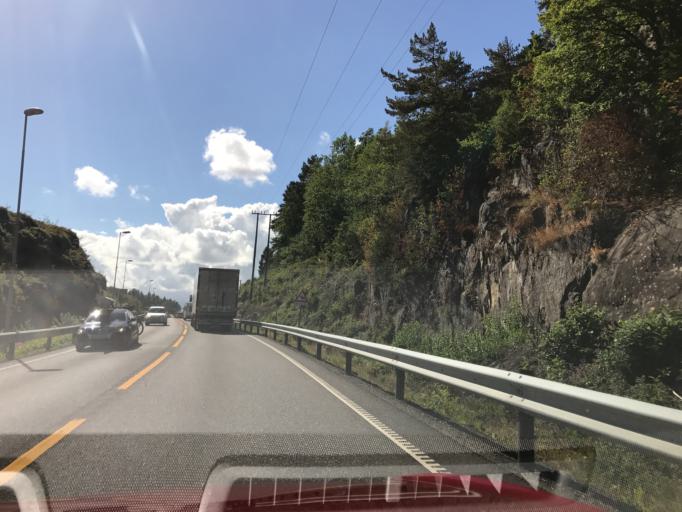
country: NO
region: Telemark
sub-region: Bamble
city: Herre
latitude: 58.9737
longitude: 9.5195
